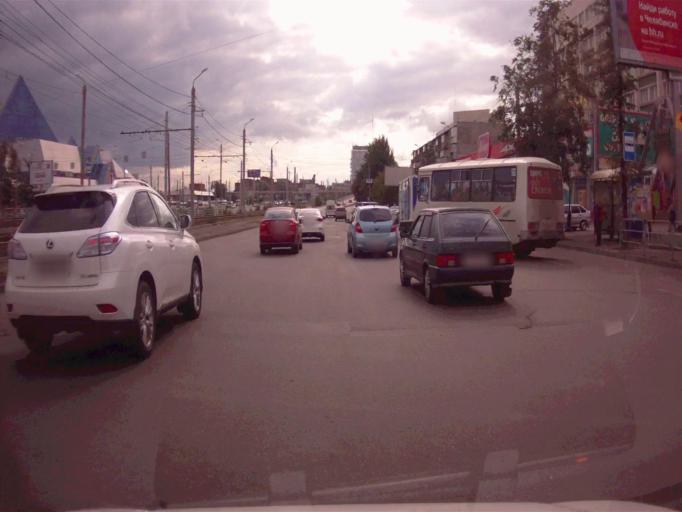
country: RU
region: Chelyabinsk
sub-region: Gorod Chelyabinsk
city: Chelyabinsk
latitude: 55.1419
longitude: 61.4127
